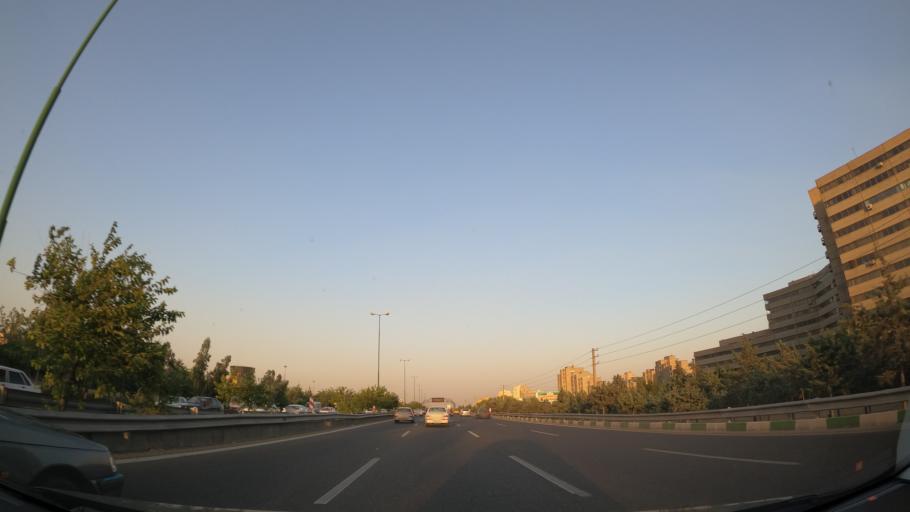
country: IR
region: Tehran
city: Tehran
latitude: 35.7157
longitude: 51.3191
